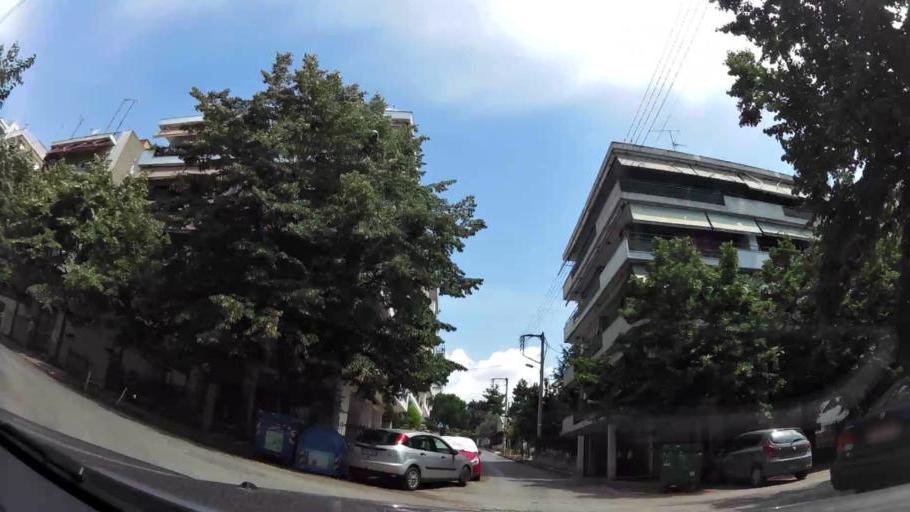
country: GR
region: Central Macedonia
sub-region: Nomos Thessalonikis
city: Triandria
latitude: 40.6181
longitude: 22.9797
